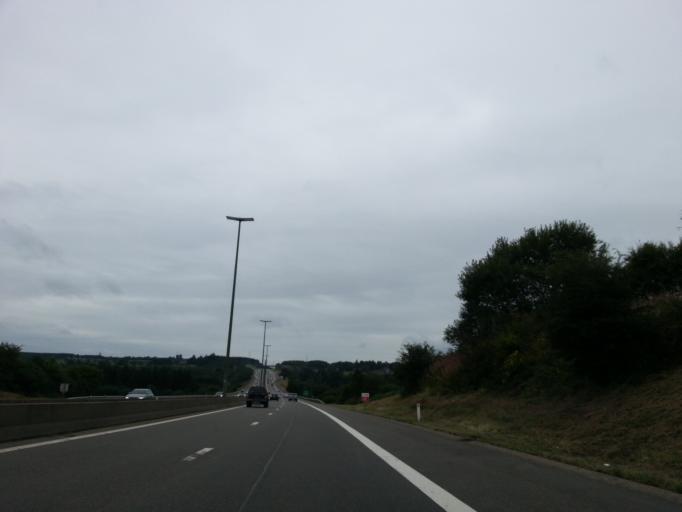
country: BE
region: Wallonia
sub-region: Province de Liege
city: Malmedy
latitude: 50.4714
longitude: 5.9833
